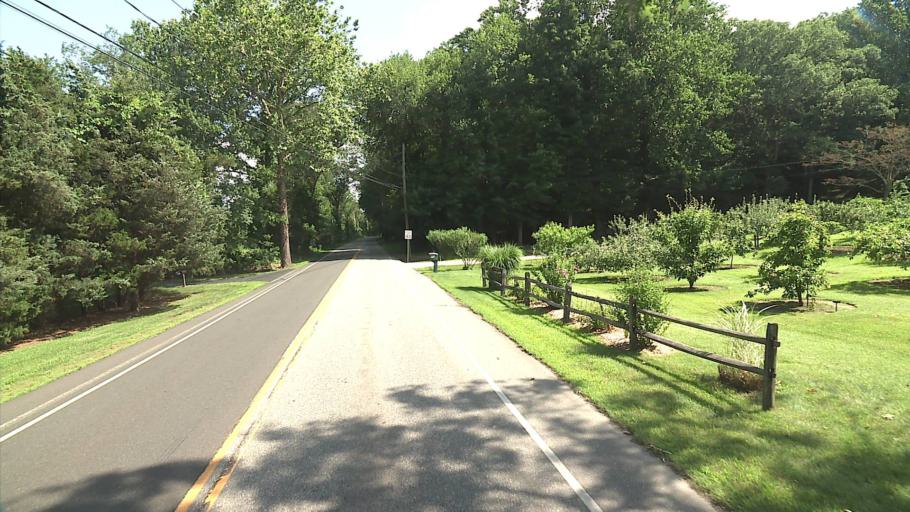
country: US
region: Connecticut
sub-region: Middlesex County
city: Westbrook Center
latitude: 41.3243
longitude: -72.4293
